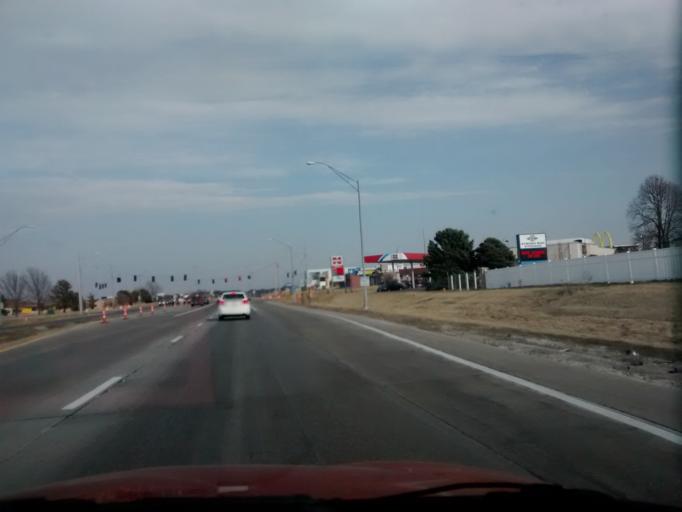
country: US
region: Nebraska
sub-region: Sarpy County
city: Papillion
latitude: 41.1399
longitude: -96.0449
